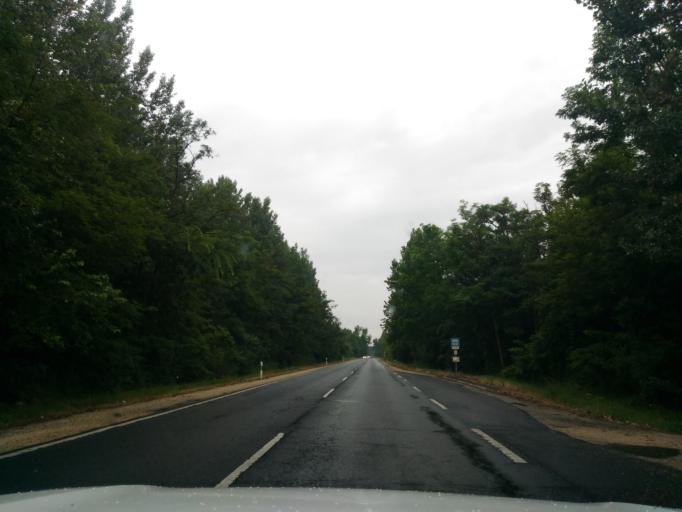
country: HU
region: Pest
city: Ocsa
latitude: 47.2693
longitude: 19.2103
